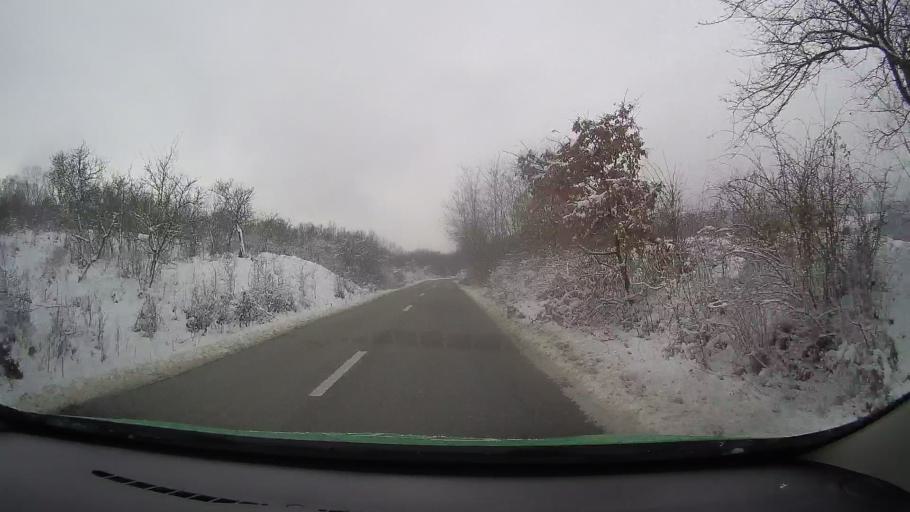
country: RO
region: Hunedoara
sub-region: Oras Hateg
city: Hateg
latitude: 45.6408
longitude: 22.9172
